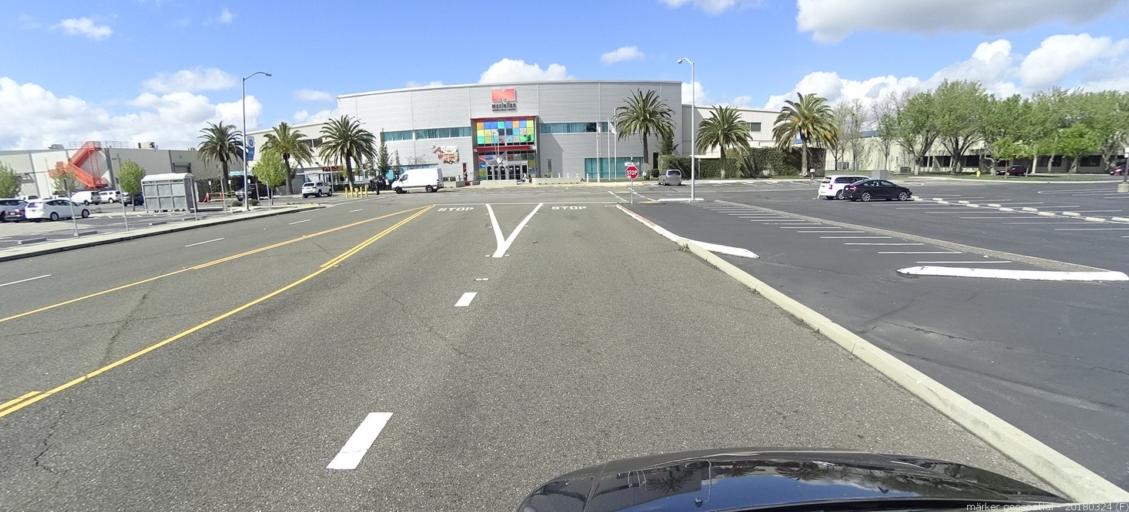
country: US
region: California
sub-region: Sacramento County
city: North Highlands
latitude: 38.6656
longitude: -121.3900
